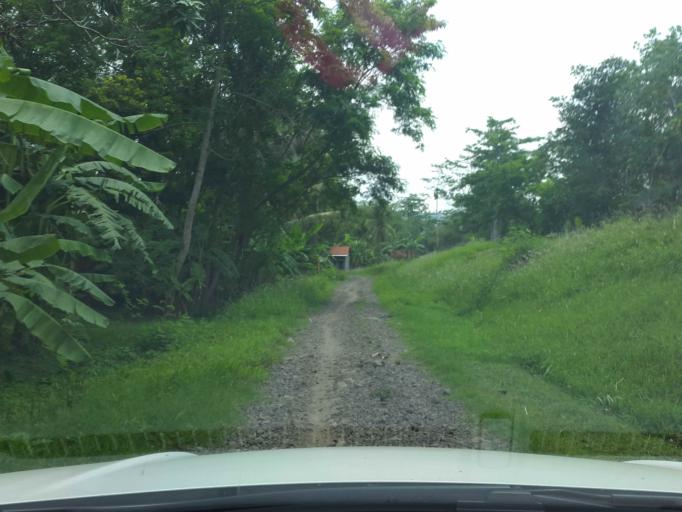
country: ID
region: West Java
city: Cintaratu
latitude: -7.3692
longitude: 108.6904
